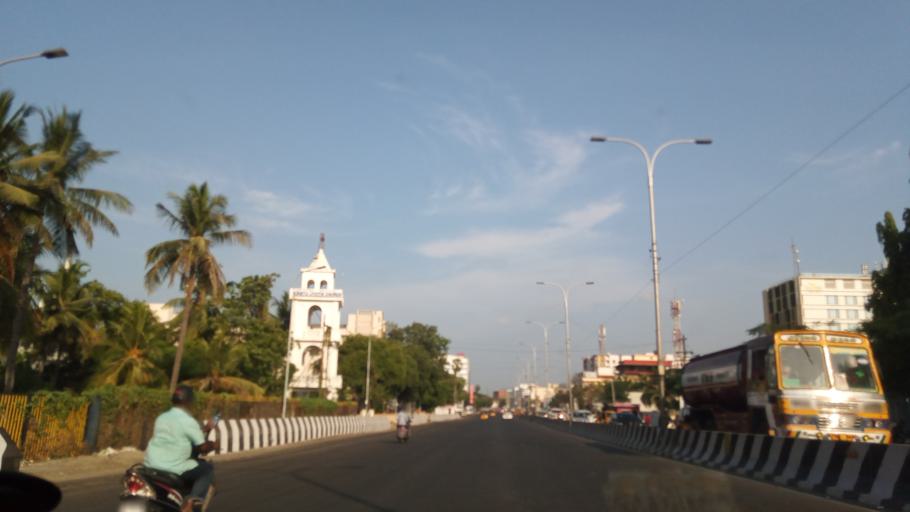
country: IN
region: Tamil Nadu
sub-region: Kancheepuram
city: Manappakkam
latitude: 13.0233
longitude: 80.1798
